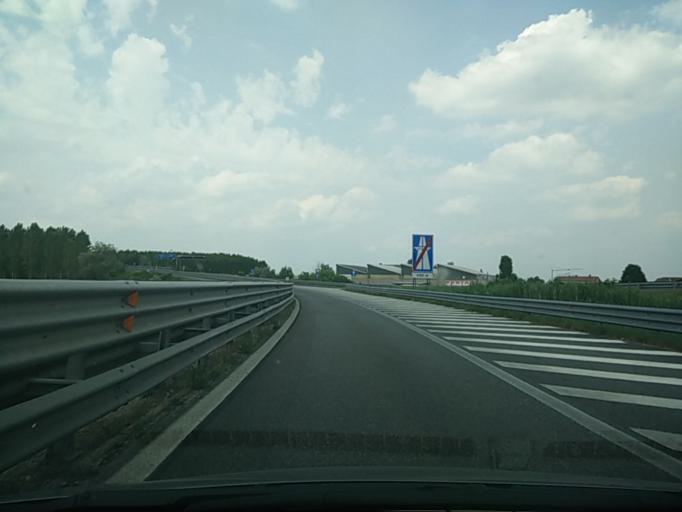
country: IT
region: Friuli Venezia Giulia
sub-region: Provincia di Pordenone
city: Fiume Veneto
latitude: 45.9386
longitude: 12.7206
